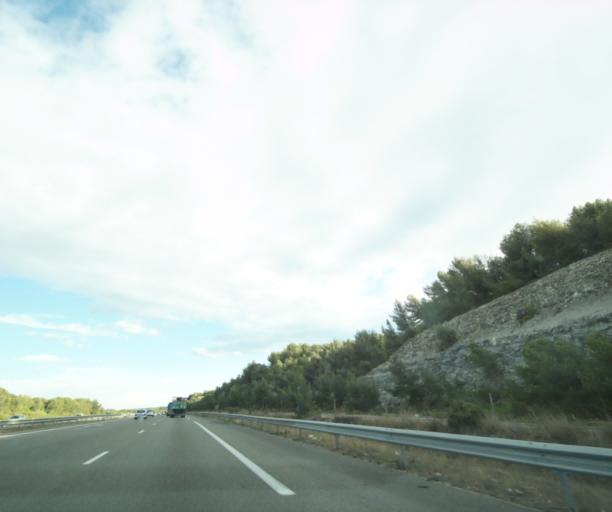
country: FR
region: Provence-Alpes-Cote d'Azur
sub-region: Departement des Bouches-du-Rhone
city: Chateauneuf-les-Martigues
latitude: 43.3895
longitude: 5.1380
